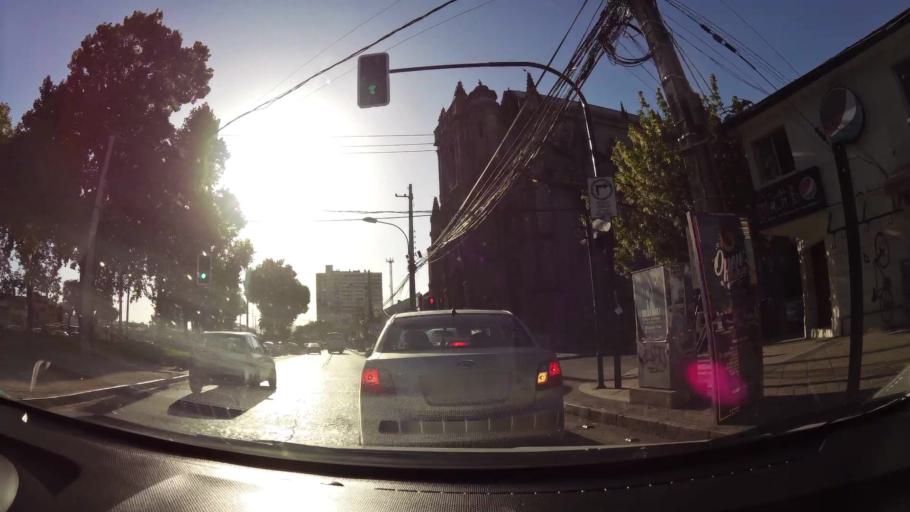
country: CL
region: Maule
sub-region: Provincia de Talca
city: Talca
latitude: -35.4289
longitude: -71.6555
